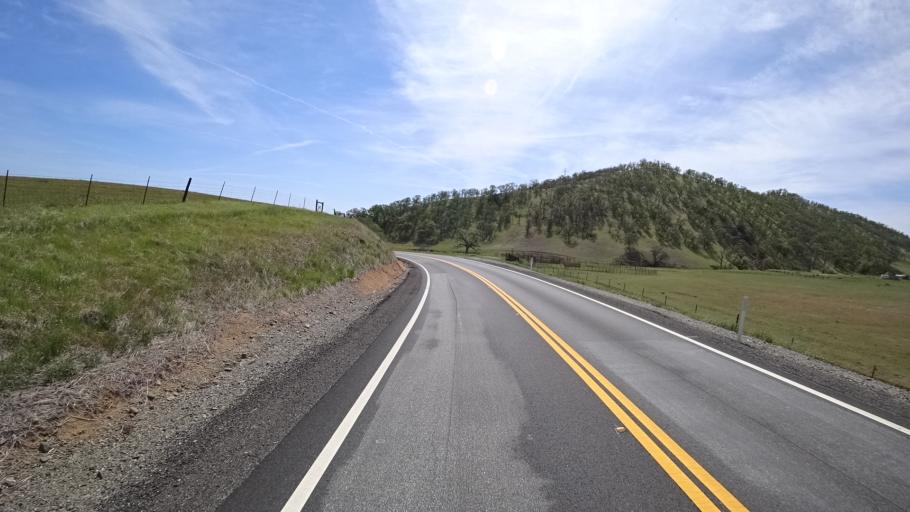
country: US
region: California
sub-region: Glenn County
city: Willows
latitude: 39.5956
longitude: -122.4657
